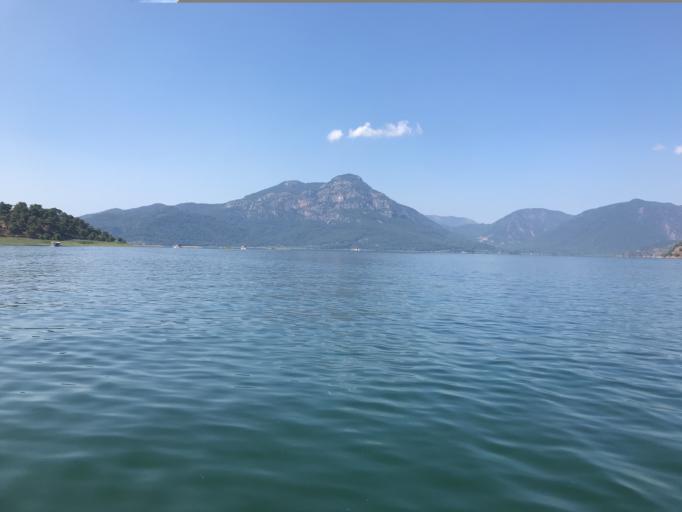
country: TR
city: Dalyan
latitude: 36.9021
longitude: 28.6462
